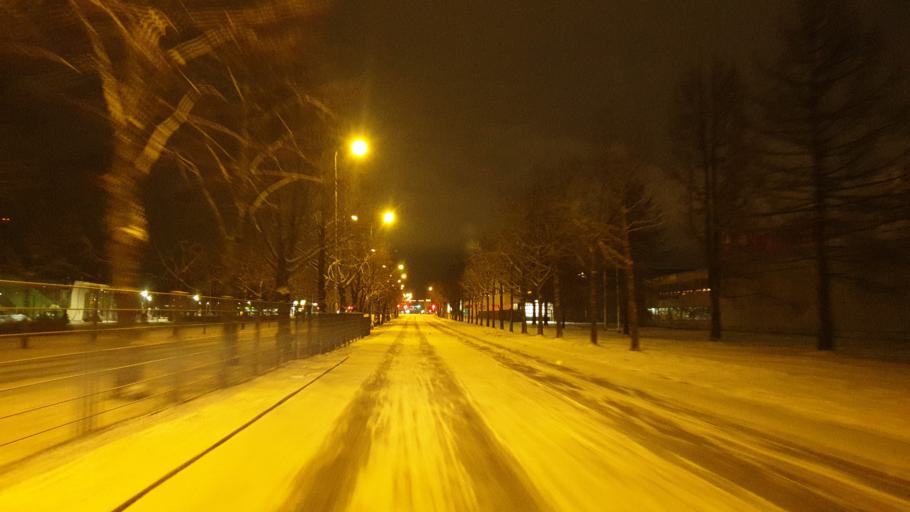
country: FI
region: Northern Ostrobothnia
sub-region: Oulu
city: Oulu
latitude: 64.9933
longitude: 25.4651
